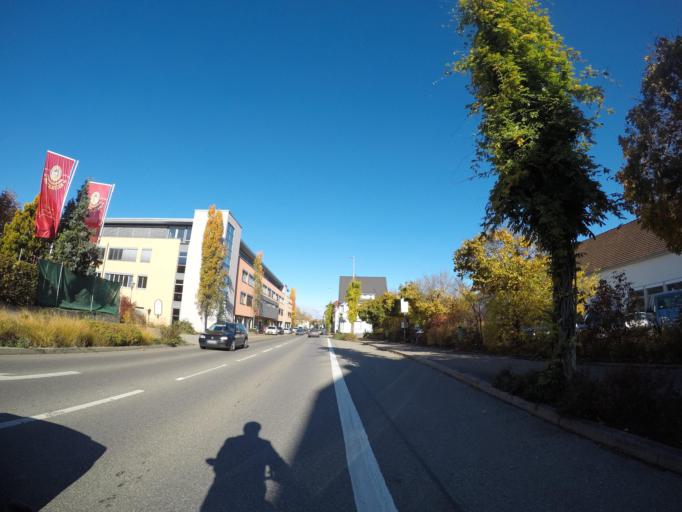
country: DE
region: Baden-Wuerttemberg
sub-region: Tuebingen Region
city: Saulgau
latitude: 48.0162
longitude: 9.5031
